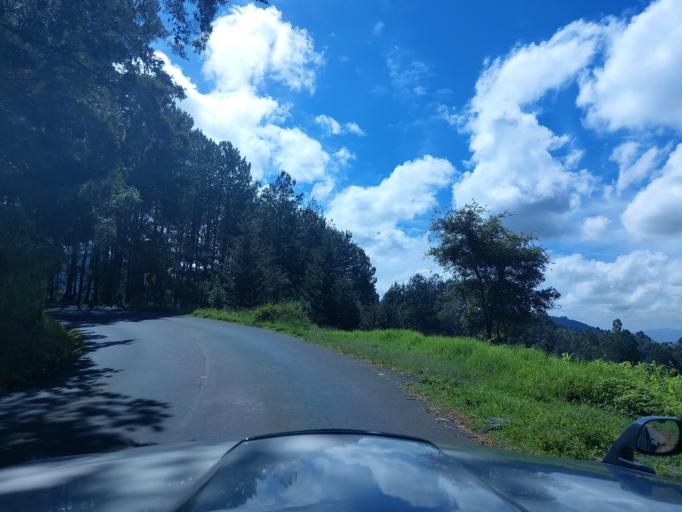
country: GT
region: Chimaltenango
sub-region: Municipio de Santa Cruz Balanya
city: Santa Cruz Balanya
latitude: 14.7060
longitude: -90.8966
